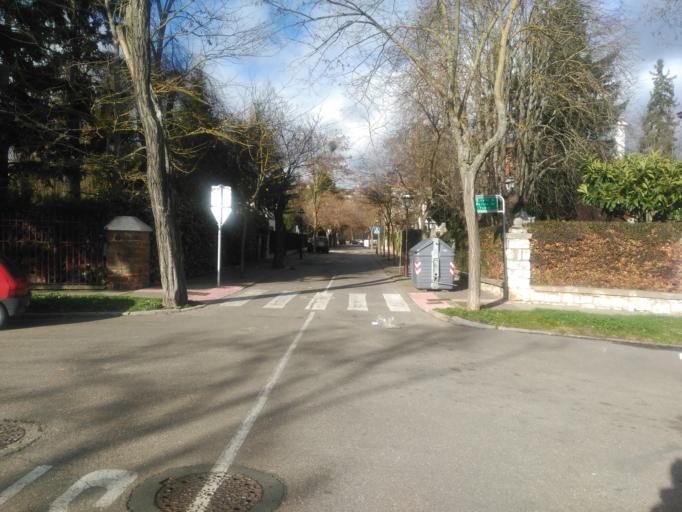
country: ES
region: Castille and Leon
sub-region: Provincia de Burgos
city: Burgos
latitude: 42.3373
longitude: -3.7143
